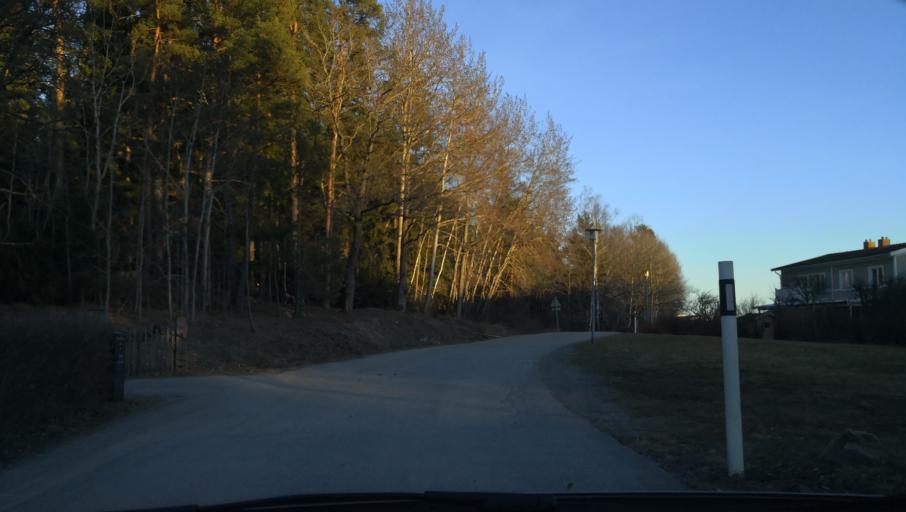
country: SE
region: Stockholm
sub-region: Varmdo Kommun
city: Gustavsberg
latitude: 59.3334
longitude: 18.4040
